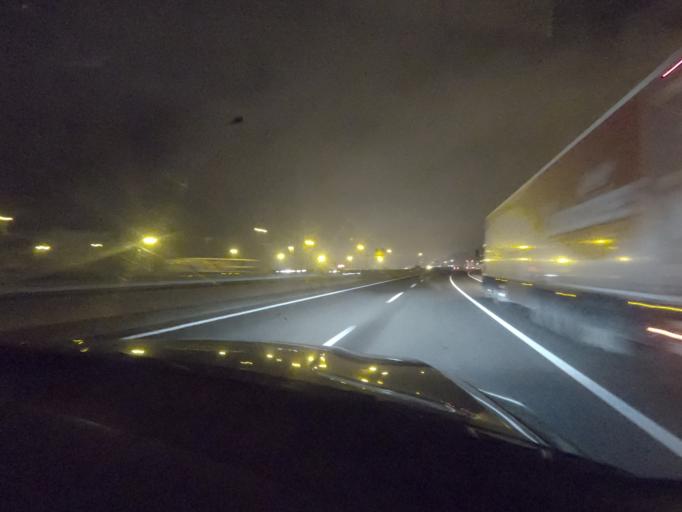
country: PT
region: Lisbon
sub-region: Vila Franca de Xira
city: Vila Franca de Xira
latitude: 38.9724
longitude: -8.9797
